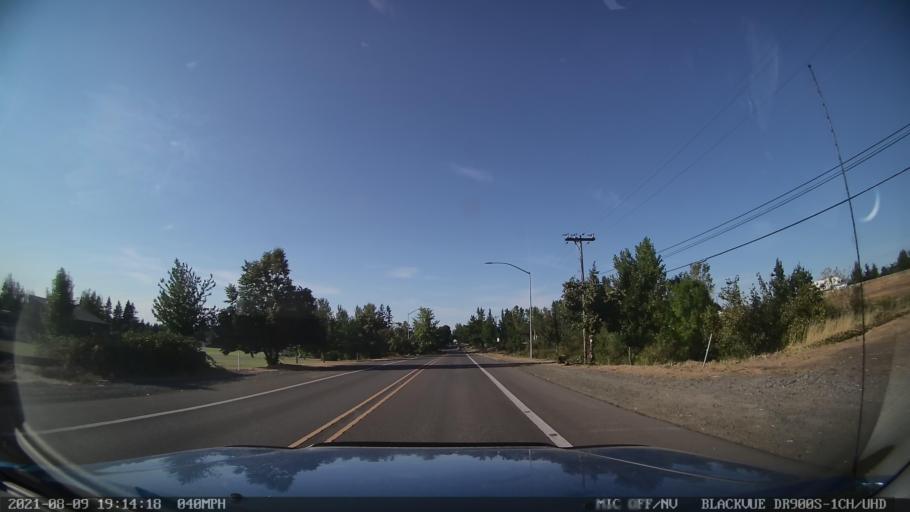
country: US
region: Oregon
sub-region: Marion County
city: Four Corners
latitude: 44.9316
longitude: -122.9917
